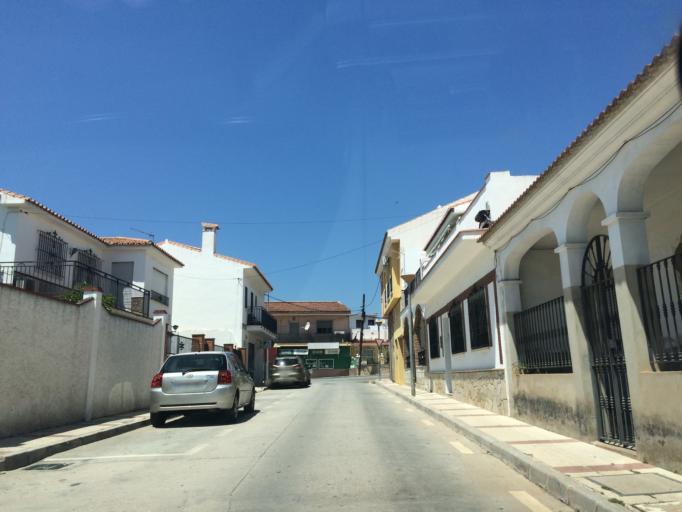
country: ES
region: Andalusia
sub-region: Provincia de Malaga
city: Malaga
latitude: 36.7352
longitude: -4.4805
